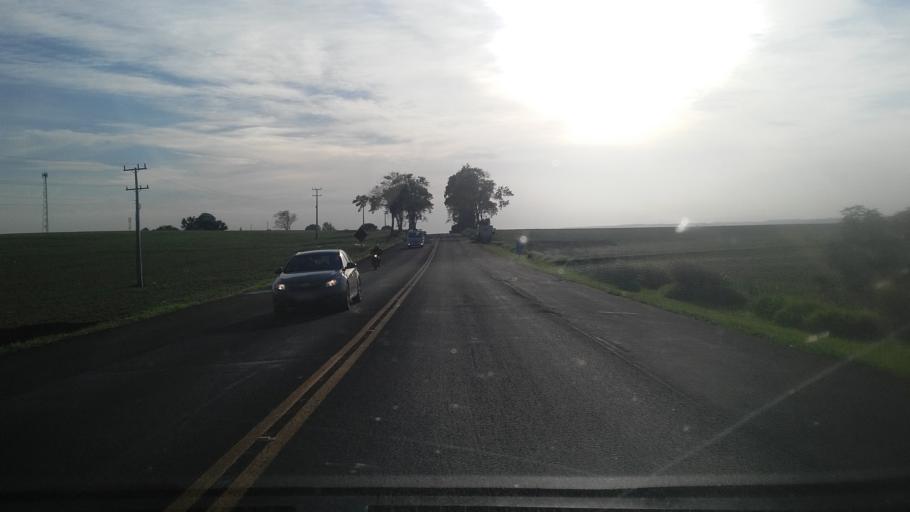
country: BR
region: Parana
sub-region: Bandeirantes
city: Bandeirantes
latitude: -23.1490
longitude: -50.5355
